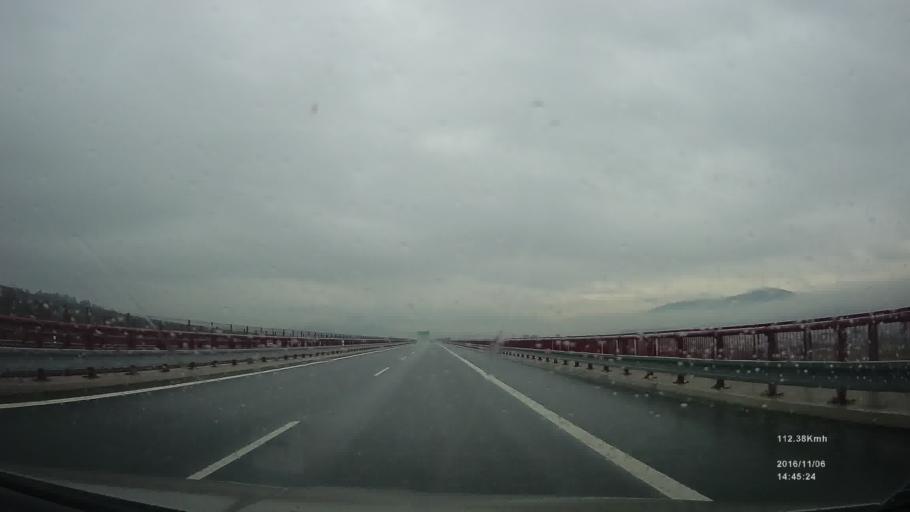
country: SK
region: Presovsky
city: Spisske Podhradie
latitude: 49.0078
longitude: 20.6777
